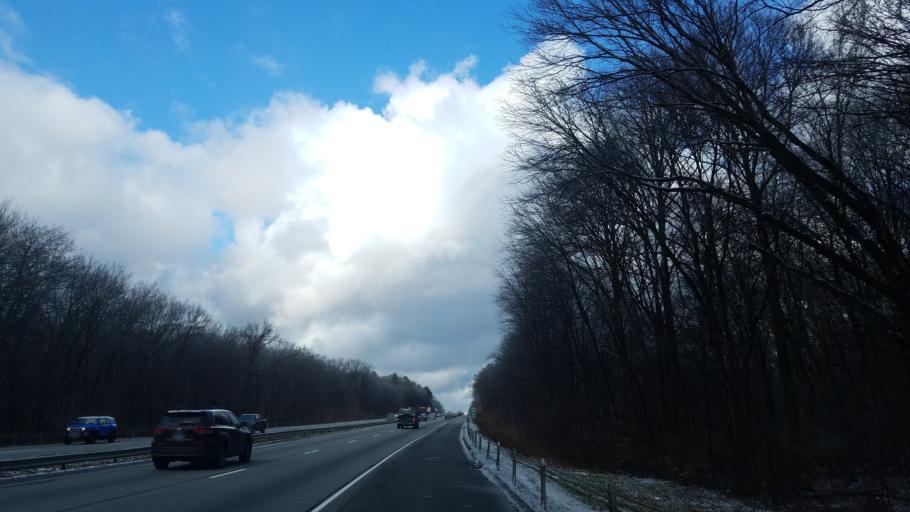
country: US
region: Connecticut
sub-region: New London County
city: Norwich
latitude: 41.5206
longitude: -72.1190
